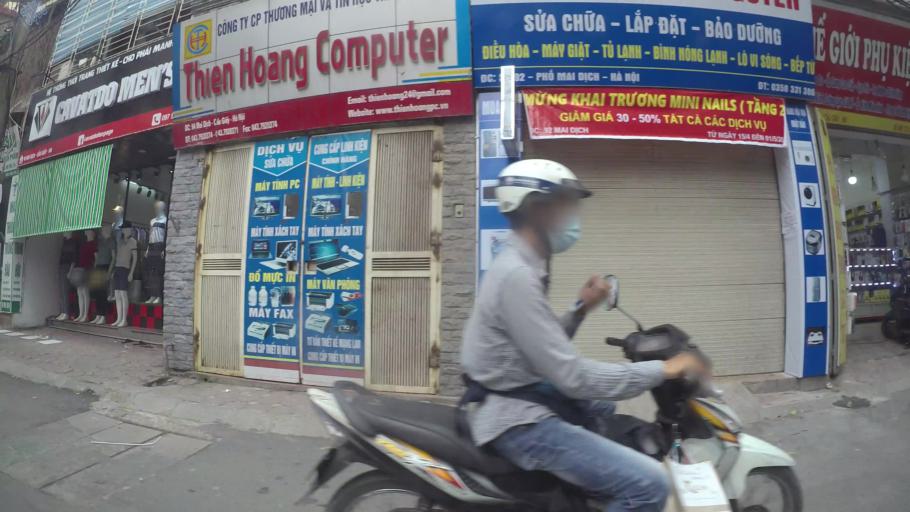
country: VN
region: Ha Noi
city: Cau Dien
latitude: 21.0415
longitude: 105.7749
